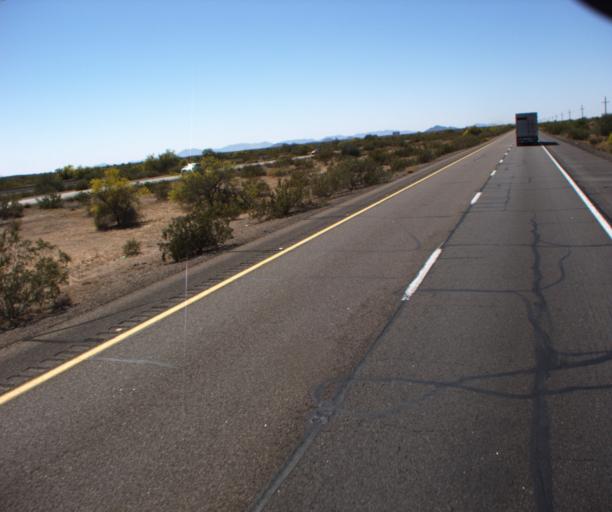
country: US
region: Arizona
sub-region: Maricopa County
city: Gila Bend
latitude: 32.8454
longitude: -113.2831
